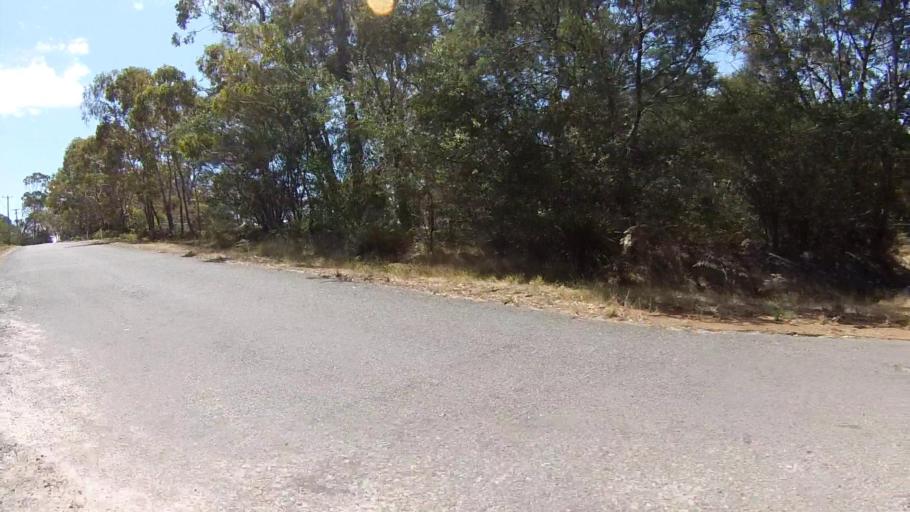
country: AU
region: Tasmania
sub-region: Clarence
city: Sandford
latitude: -42.9920
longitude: 147.4777
